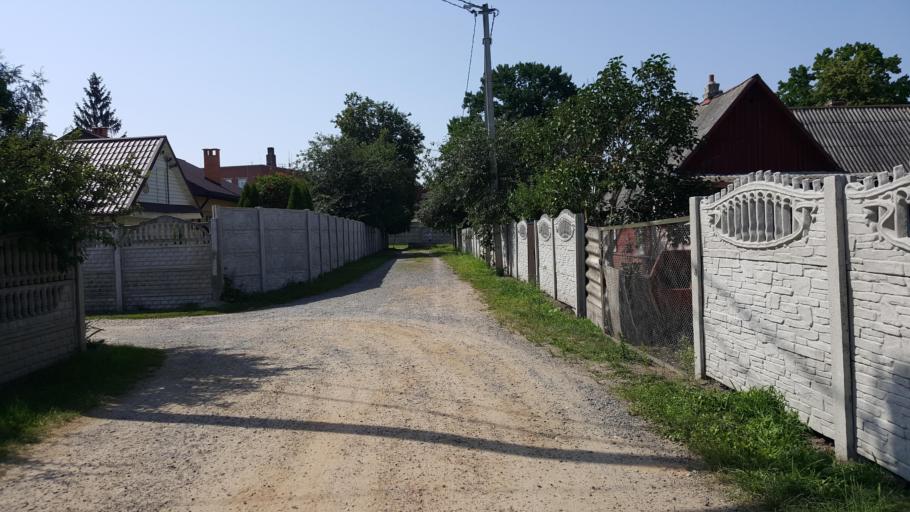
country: BY
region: Brest
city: Zhabinka
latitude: 52.2014
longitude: 24.0216
